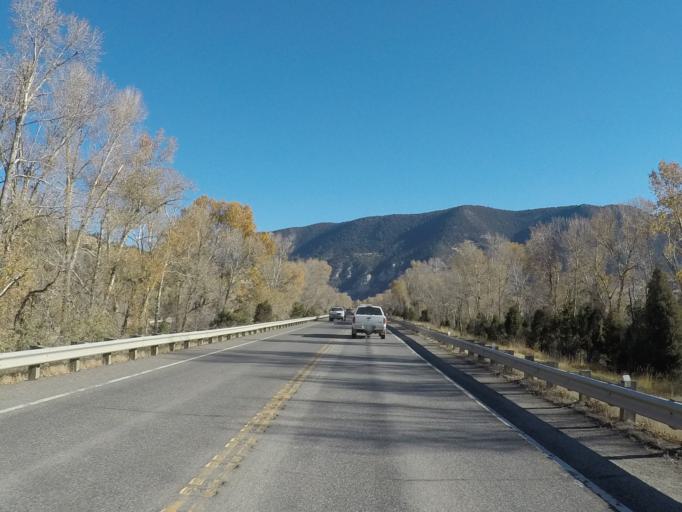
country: US
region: Montana
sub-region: Park County
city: Livingston
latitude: 45.5780
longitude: -110.5832
